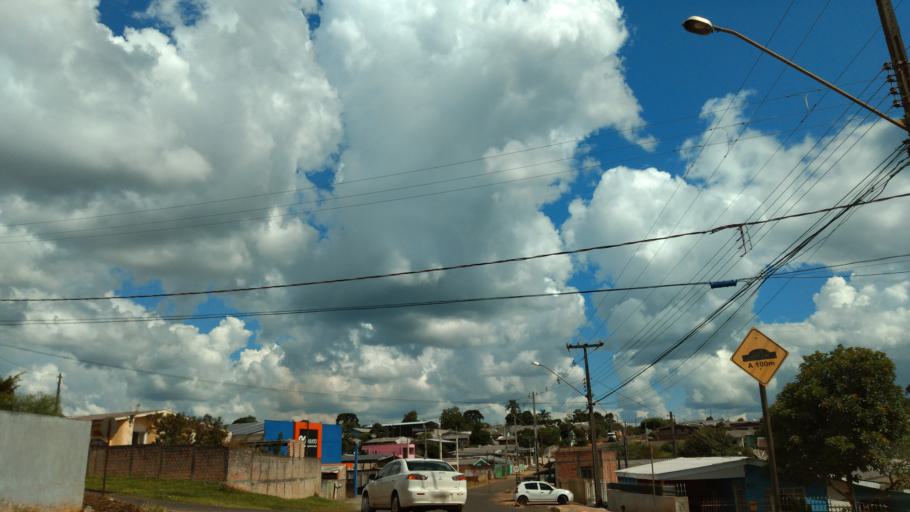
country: BR
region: Parana
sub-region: Guarapuava
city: Guarapuava
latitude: -25.4074
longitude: -51.4921
